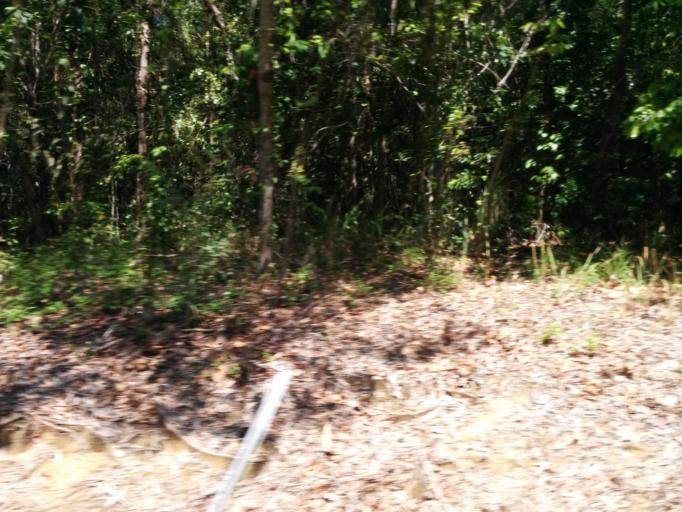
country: AU
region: Queensland
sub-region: Cairns
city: Palm Cove
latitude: -16.6738
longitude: 145.5683
